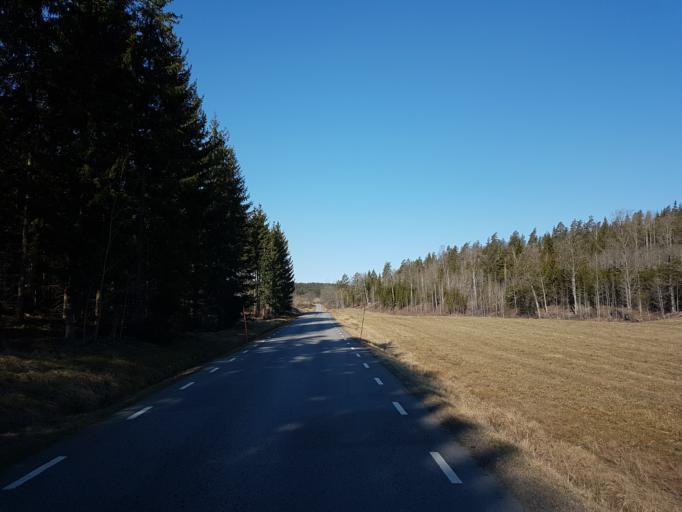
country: SE
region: OEstergoetland
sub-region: Valdemarsviks Kommun
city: Gusum
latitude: 58.1991
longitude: 16.3623
